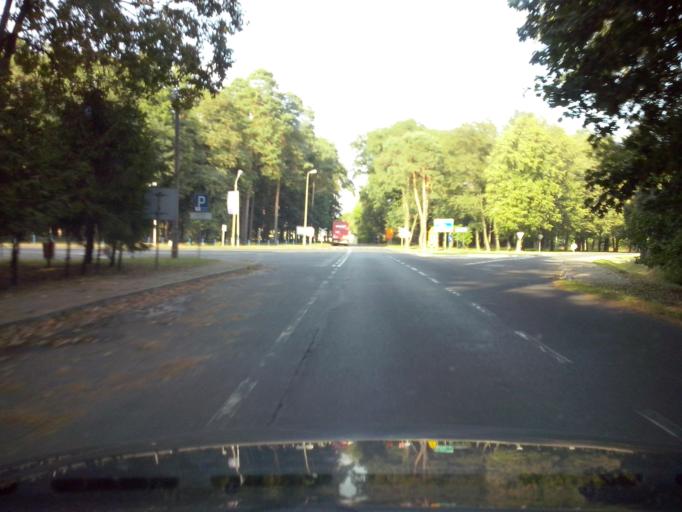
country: PL
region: Subcarpathian Voivodeship
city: Nowa Sarzyna
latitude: 50.3264
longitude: 22.3352
